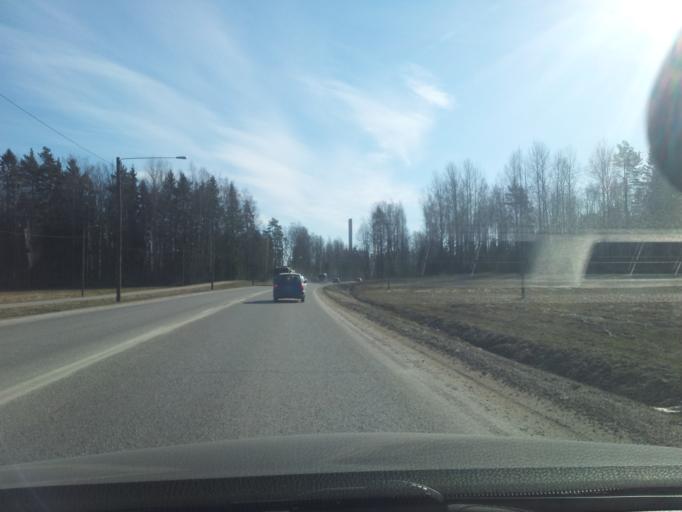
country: FI
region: Uusimaa
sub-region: Helsinki
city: Espoo
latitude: 60.1664
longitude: 24.6244
